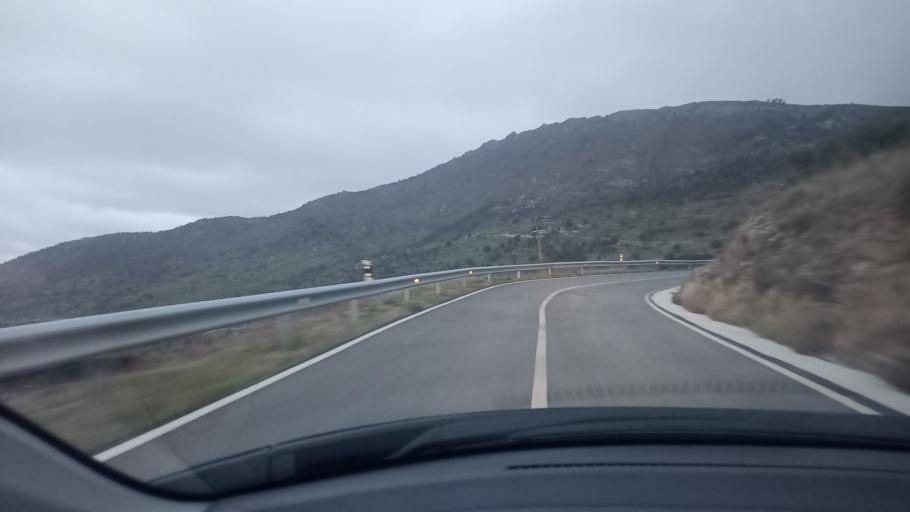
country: ES
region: Madrid
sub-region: Provincia de Madrid
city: Zarzalejo
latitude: 40.5558
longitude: -4.1954
